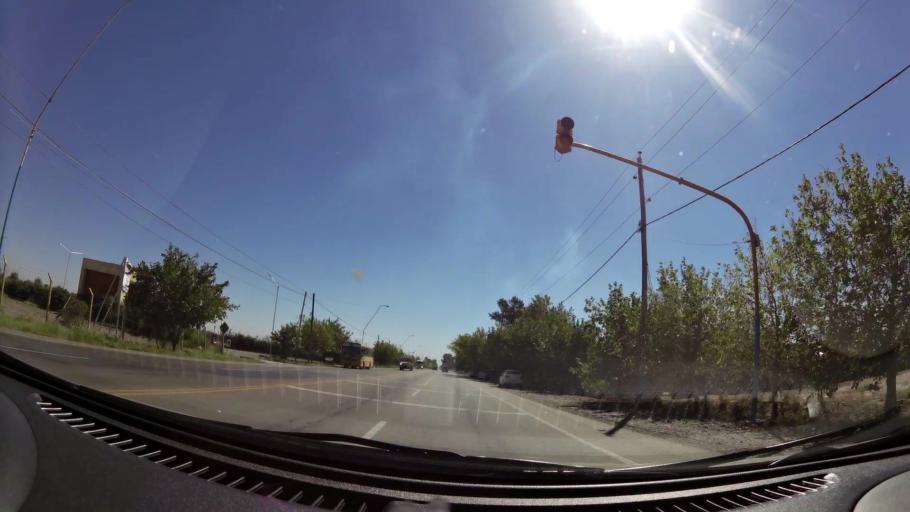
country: AR
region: San Juan
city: Villa Aberastain
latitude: -31.6236
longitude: -68.5516
